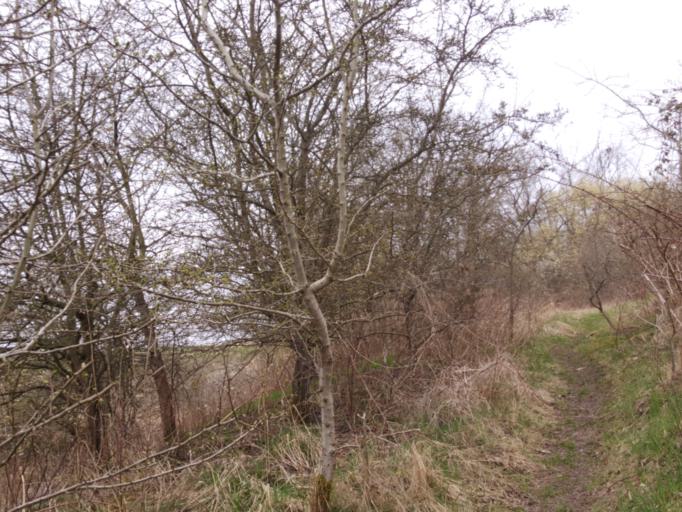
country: DE
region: Hamburg
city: Wandsbek
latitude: 53.5041
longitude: 10.1095
